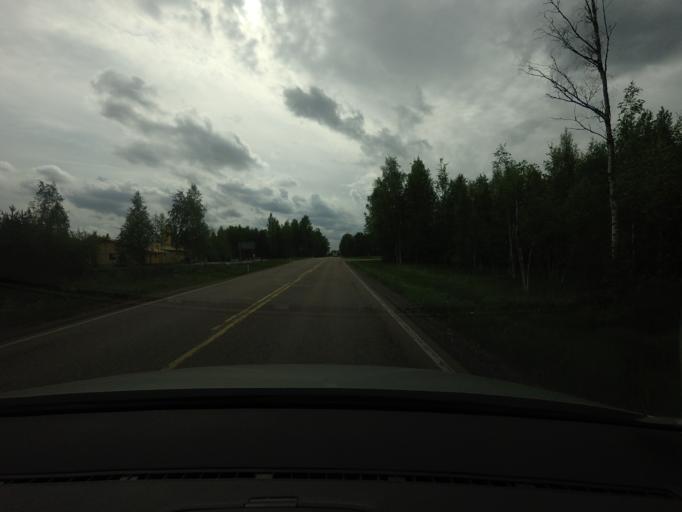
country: FI
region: South Karelia
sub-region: Lappeenranta
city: Taavetti
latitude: 60.9087
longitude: 27.5652
